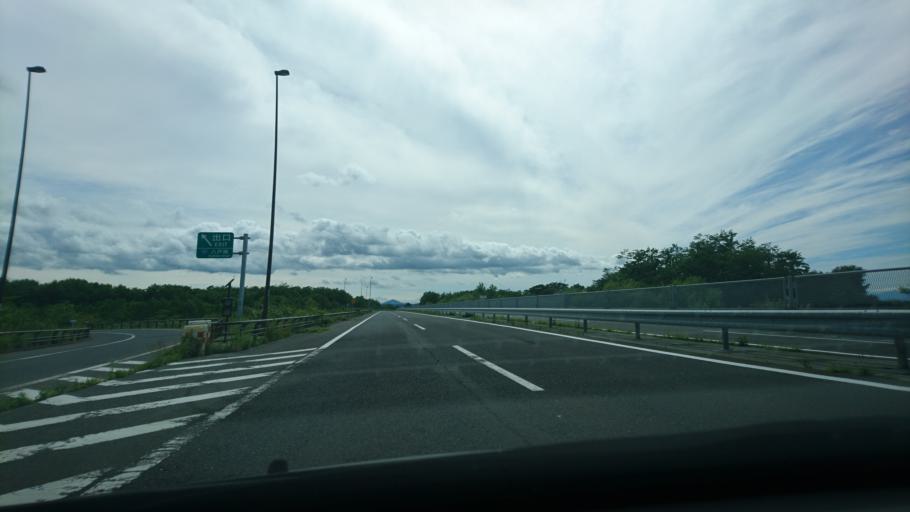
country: JP
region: Aomori
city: Hachinohe
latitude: 40.4815
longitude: 141.5577
